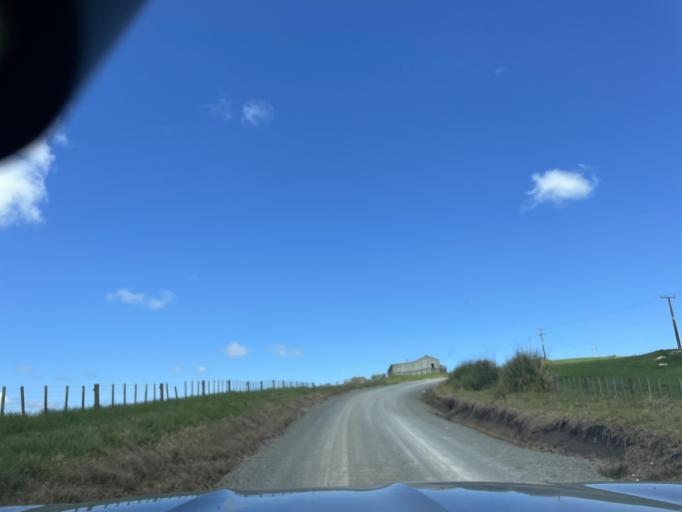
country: NZ
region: Auckland
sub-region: Auckland
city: Wellsford
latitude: -36.2867
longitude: 174.3524
